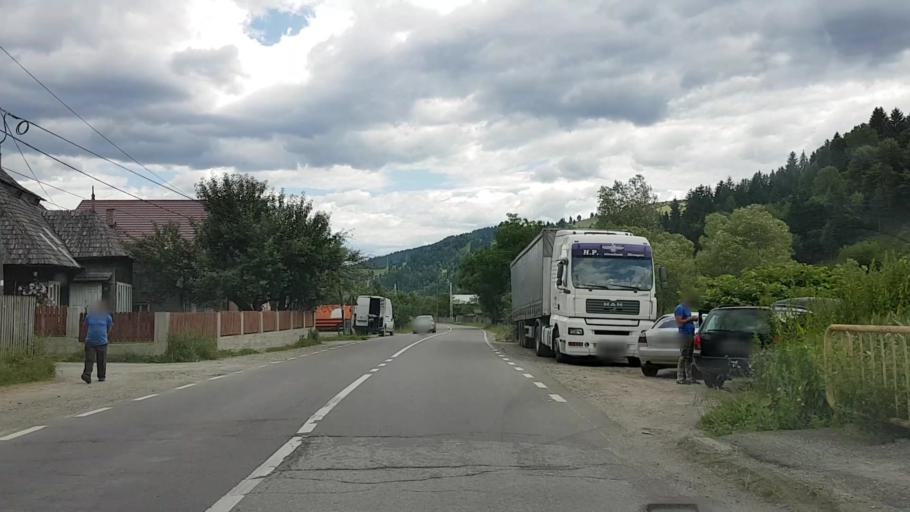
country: RO
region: Neamt
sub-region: Comuna Farcasa
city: Farcasa
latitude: 47.1647
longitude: 25.8098
